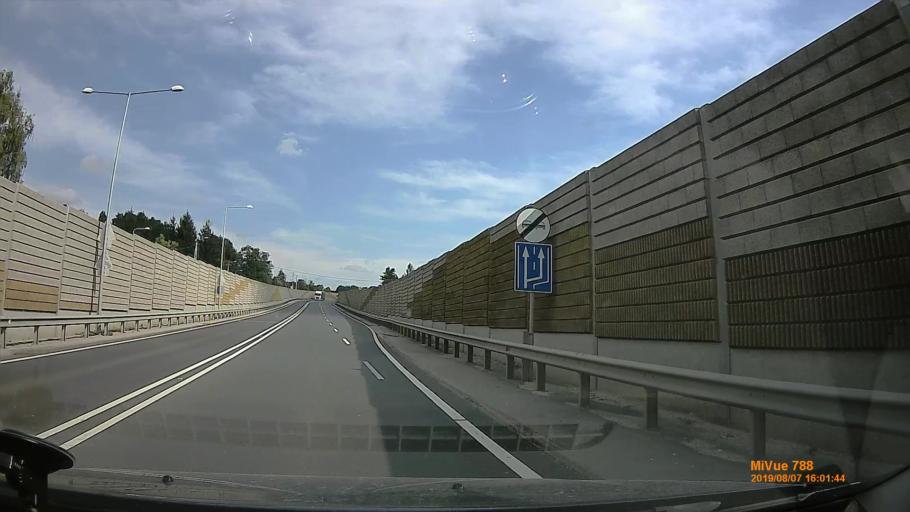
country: HU
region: Vas
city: Kormend
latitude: 46.9868
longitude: 16.6199
